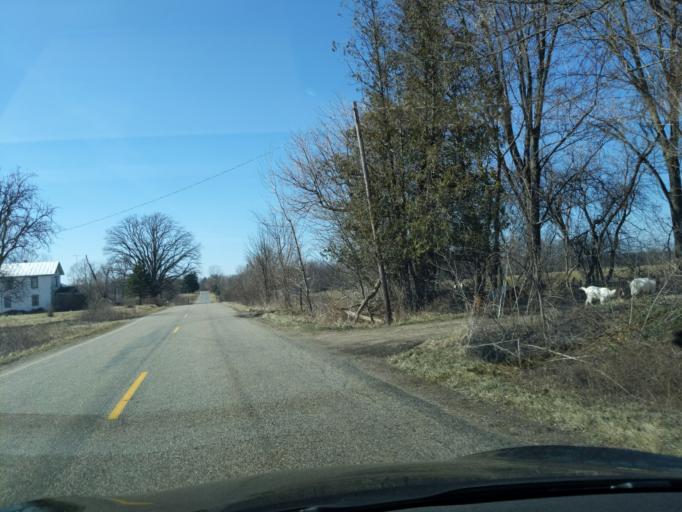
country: US
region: Michigan
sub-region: Ionia County
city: Lake Odessa
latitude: 42.7125
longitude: -85.0722
